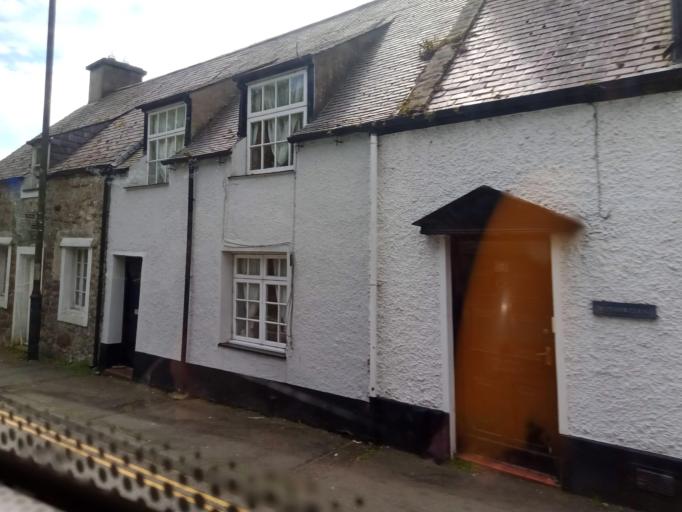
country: GB
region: Wales
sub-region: Anglesey
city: Beaumaris
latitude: 53.2650
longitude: -4.0962
